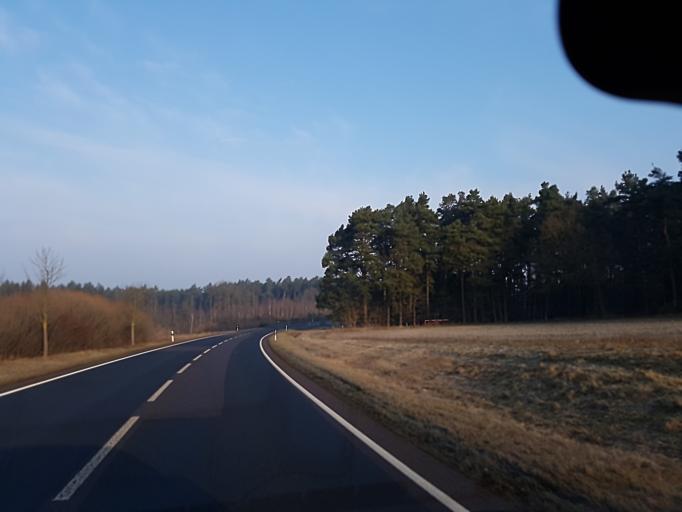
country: DE
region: Brandenburg
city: Wiesenburg
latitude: 52.0826
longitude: 12.4467
